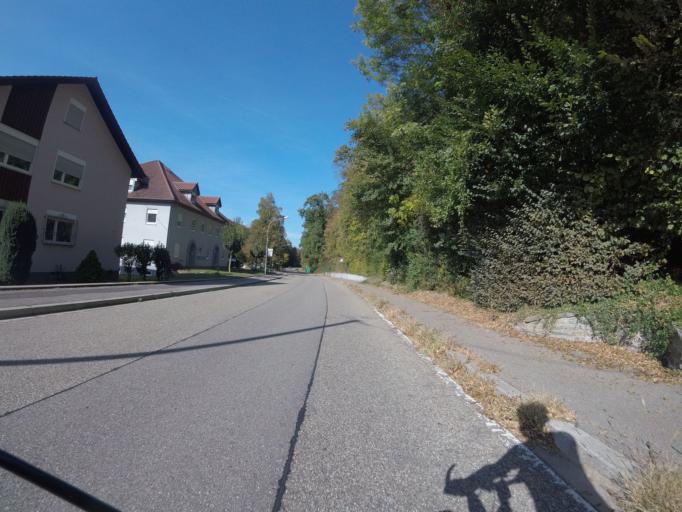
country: DE
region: Baden-Wuerttemberg
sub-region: Karlsruhe Region
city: Bretten
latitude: 49.0114
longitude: 8.7235
